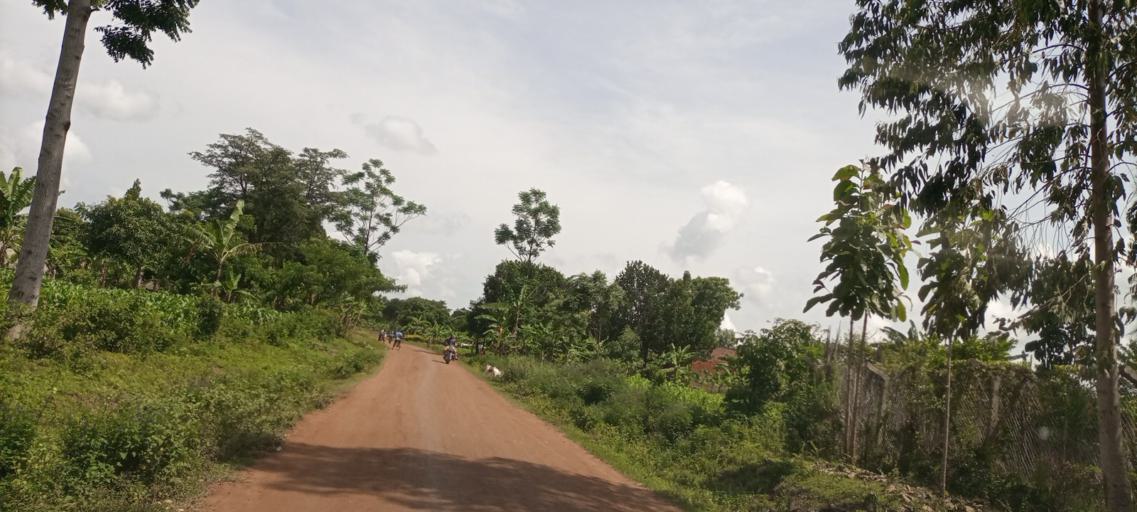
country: UG
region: Eastern Region
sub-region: Budaka District
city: Budaka
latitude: 1.1733
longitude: 33.9306
